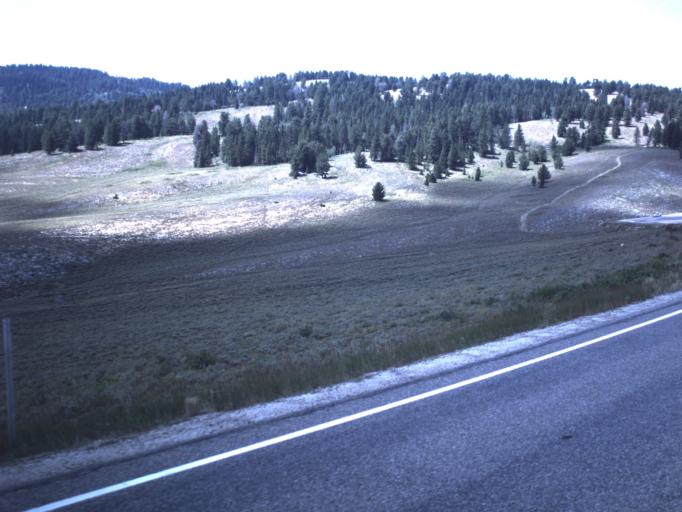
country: US
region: Idaho
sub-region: Bear Lake County
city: Paris
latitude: 41.9308
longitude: -111.4795
